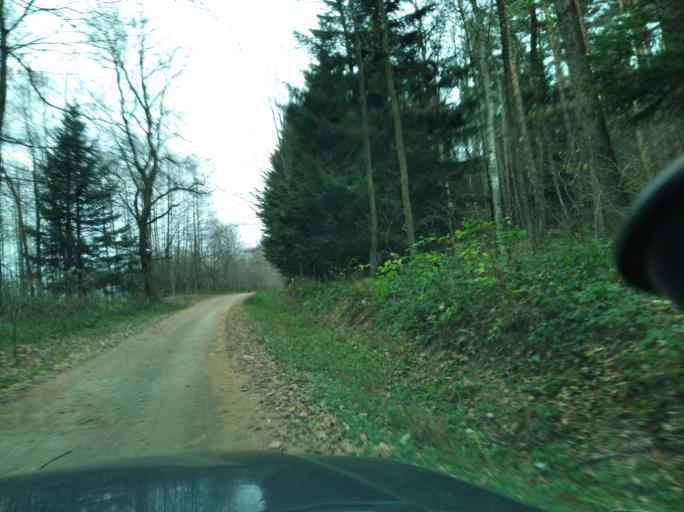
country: PL
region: Subcarpathian Voivodeship
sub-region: Powiat strzyzowski
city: Wysoka Strzyzowska
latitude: 49.7932
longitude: 21.7687
